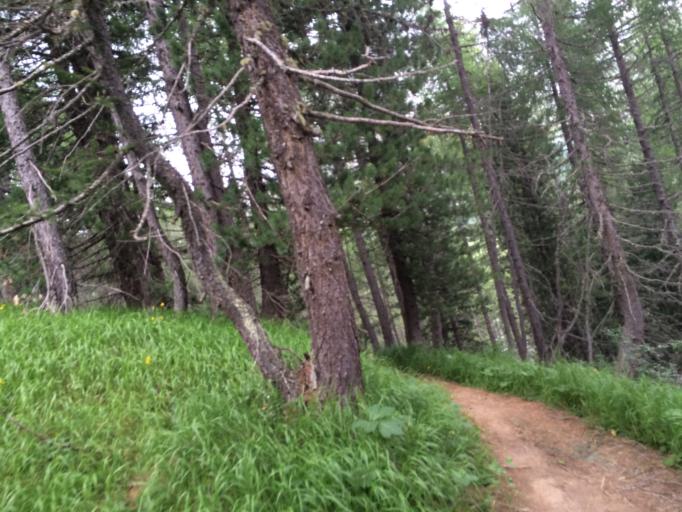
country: IT
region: Veneto
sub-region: Provincia di Belluno
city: Colle Santa Lucia
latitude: 46.5165
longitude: 12.0196
